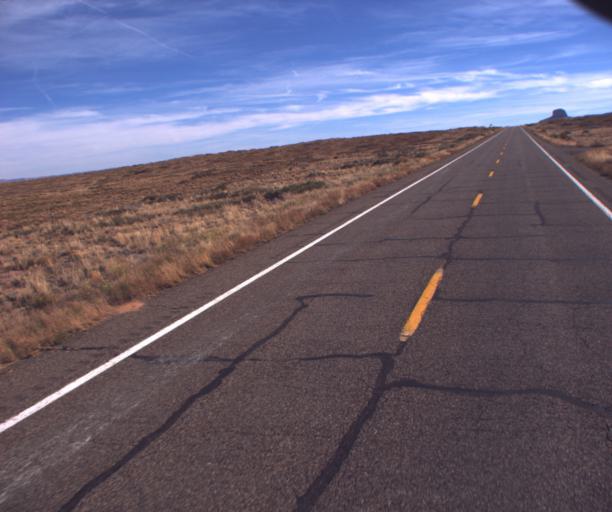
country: US
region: Arizona
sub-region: Coconino County
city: Kaibito
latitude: 36.6122
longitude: -111.0233
